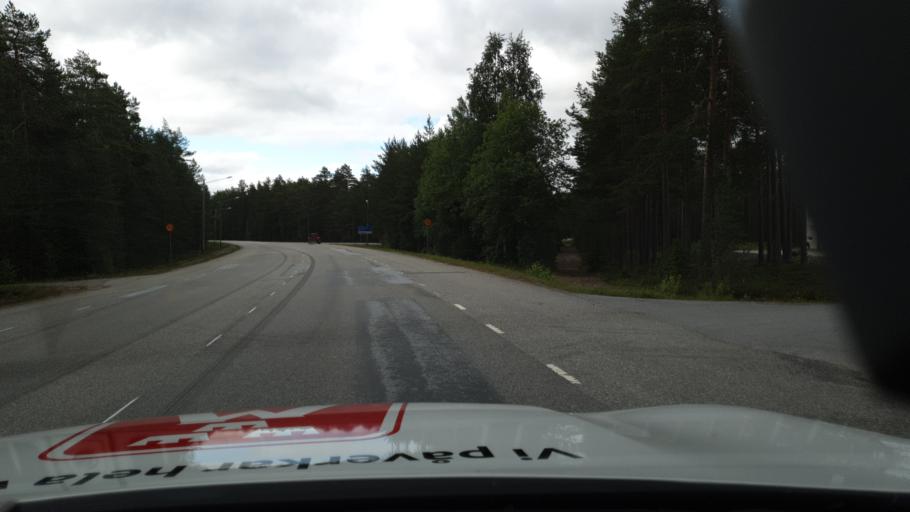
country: SE
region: Vaesterbotten
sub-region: Umea Kommun
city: Roback
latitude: 63.7624
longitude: 20.2089
